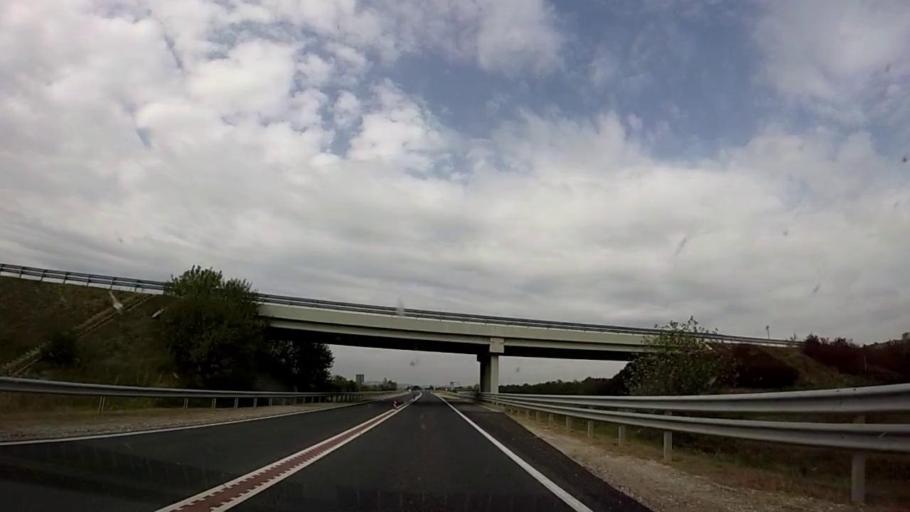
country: HR
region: Medimurska
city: Domasinec
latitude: 46.5004
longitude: 16.6173
